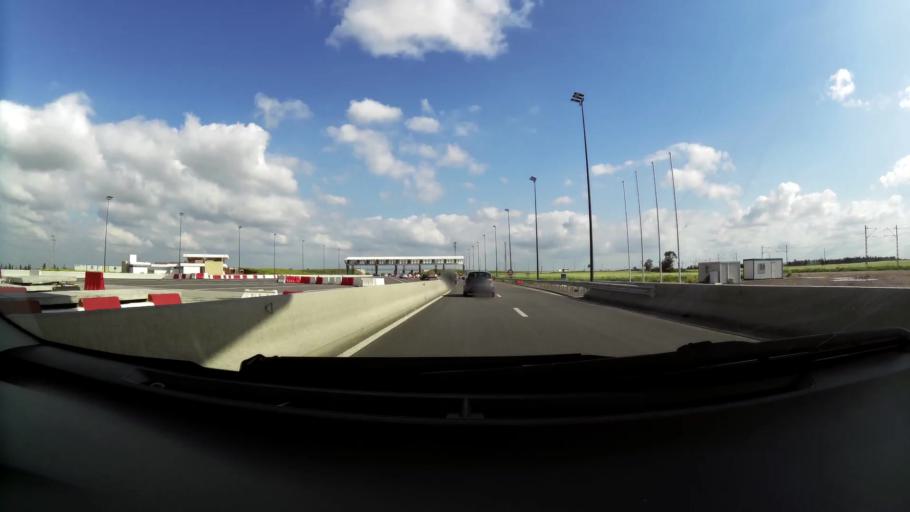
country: MA
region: Chaouia-Ouardigha
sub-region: Settat Province
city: Berrechid
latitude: 33.3203
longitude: -7.6048
